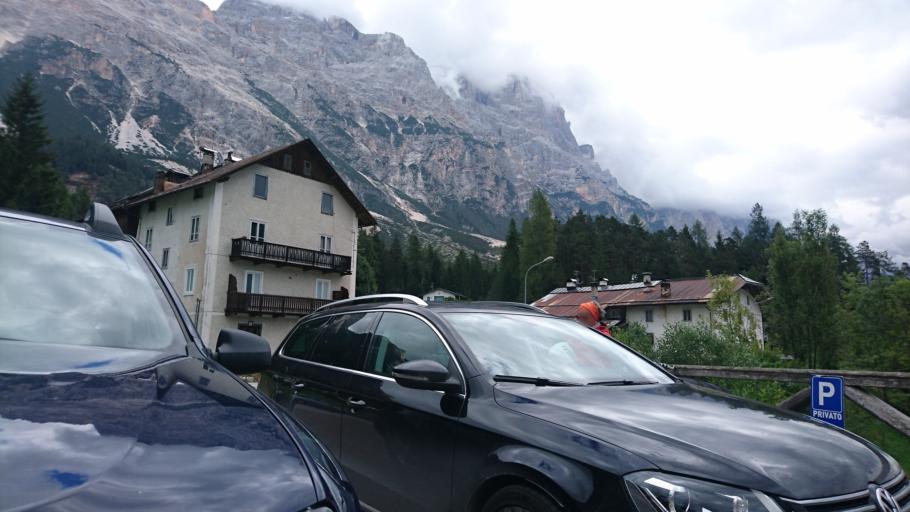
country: IT
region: Veneto
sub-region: Provincia di Belluno
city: Cortina d'Ampezzo
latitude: 46.5063
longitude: 12.1586
